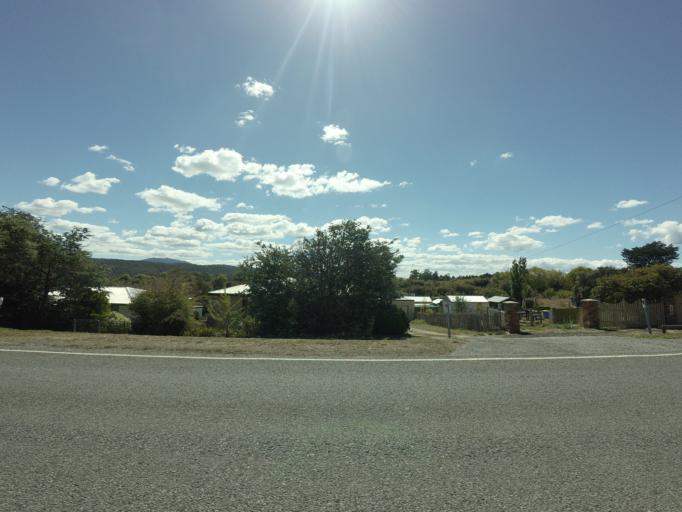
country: AU
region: Tasmania
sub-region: Break O'Day
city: St Helens
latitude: -41.6377
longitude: 147.9737
